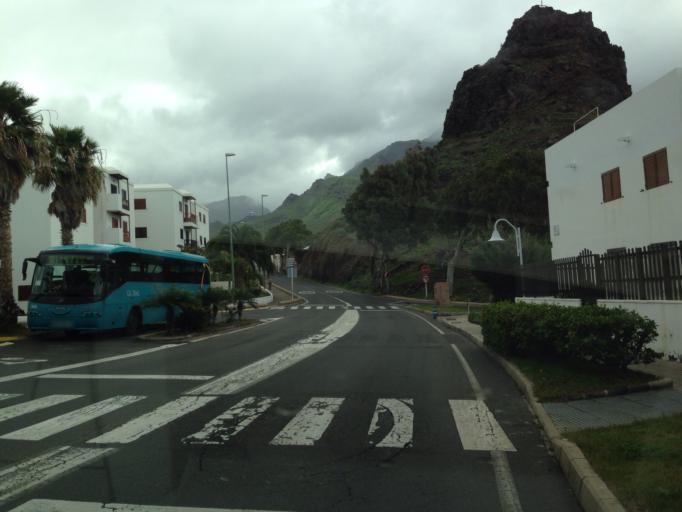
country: ES
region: Canary Islands
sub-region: Provincia de Las Palmas
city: Agaete
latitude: 28.1025
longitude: -15.7100
